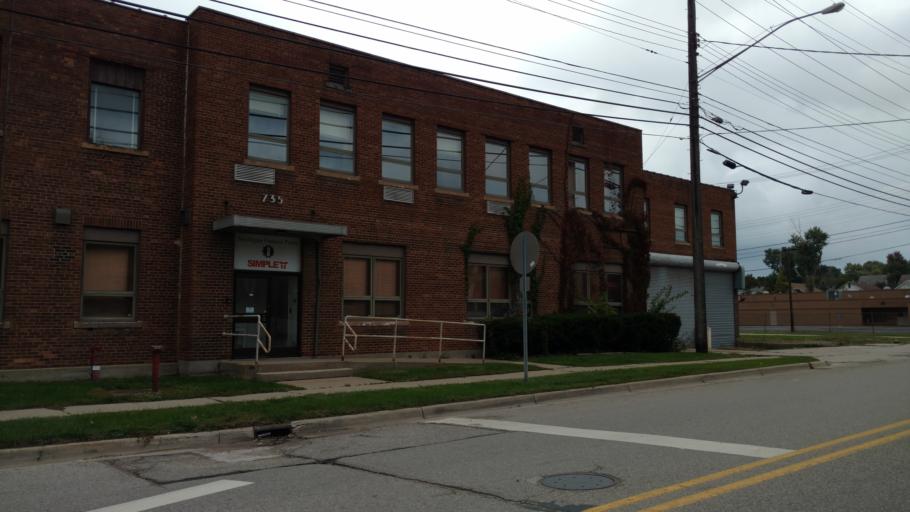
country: US
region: Michigan
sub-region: Ingham County
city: Lansing
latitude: 42.7232
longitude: -84.5418
